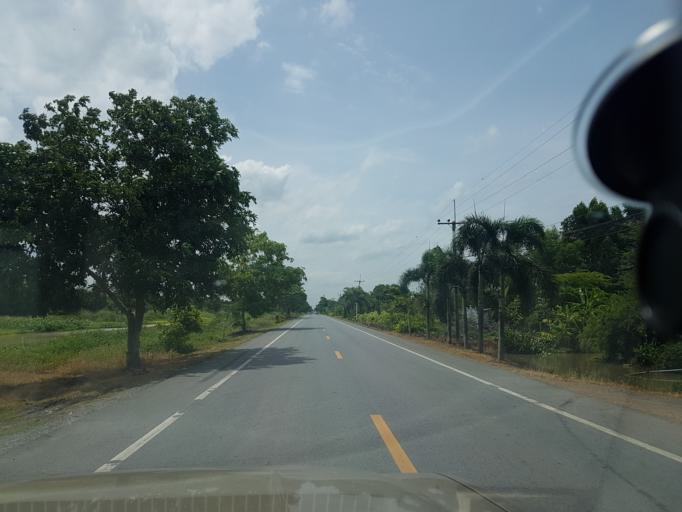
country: TH
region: Pathum Thani
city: Nong Suea
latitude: 14.2148
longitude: 100.8920
